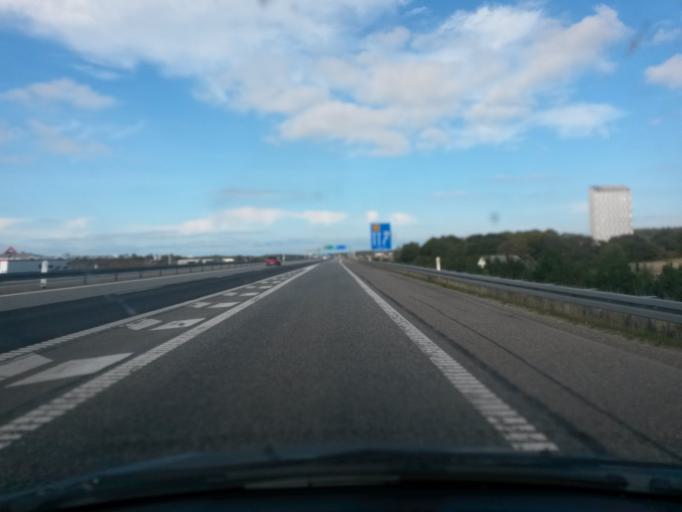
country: DK
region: Central Jutland
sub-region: Herning Kommune
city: Gjellerup Kirkeby
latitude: 56.1305
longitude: 9.0128
